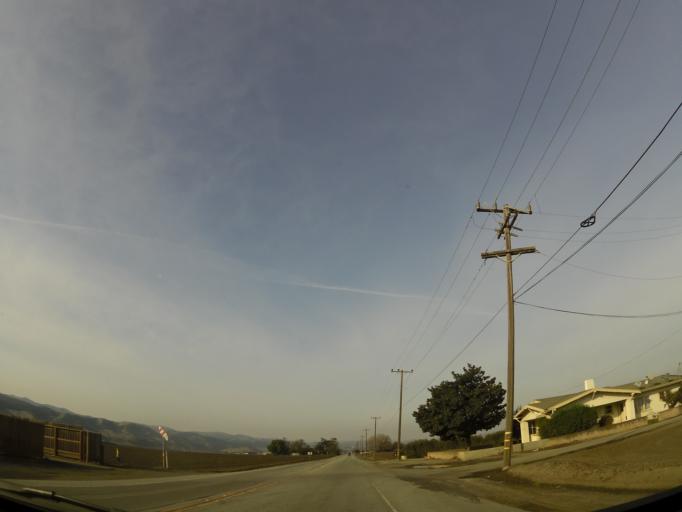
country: US
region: California
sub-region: San Benito County
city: San Juan Bautista
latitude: 36.8416
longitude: -121.4721
